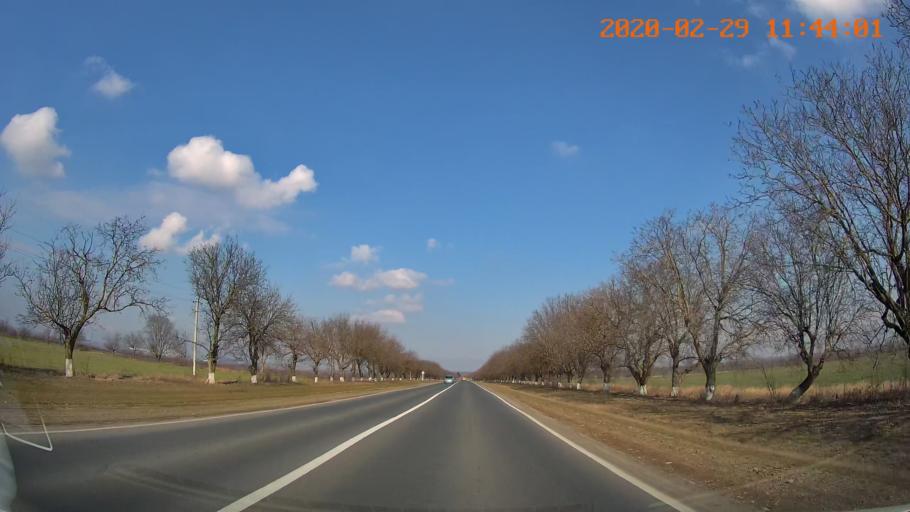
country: MD
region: Rezina
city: Saharna
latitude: 47.7051
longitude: 29.0011
